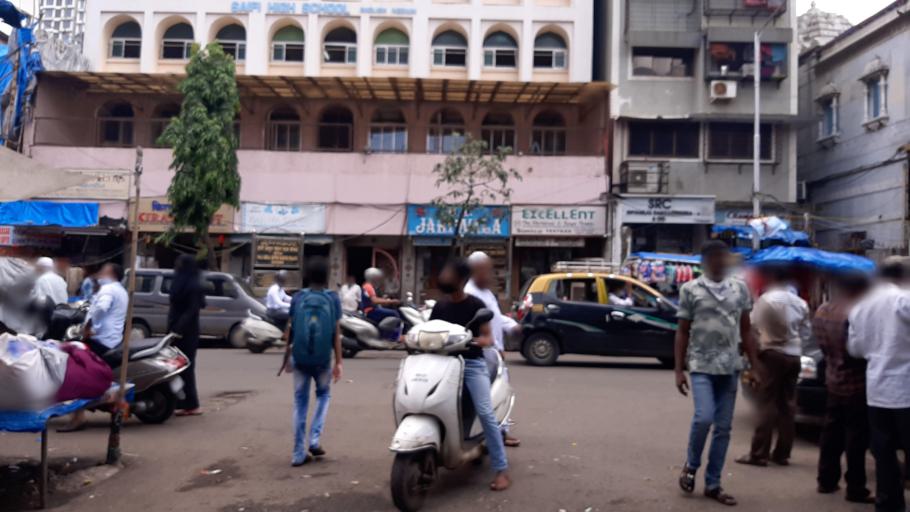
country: IN
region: Maharashtra
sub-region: Mumbai Suburban
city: Mumbai
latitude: 18.9549
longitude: 72.8320
